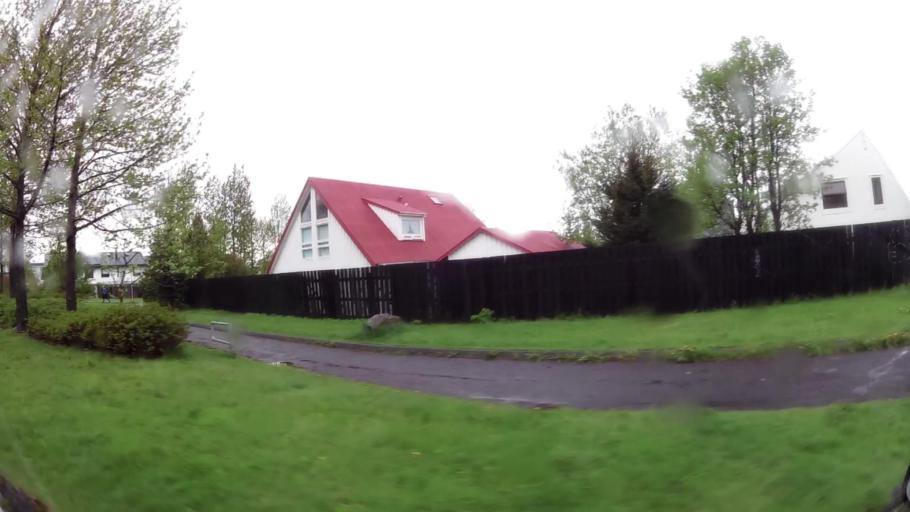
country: IS
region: Capital Region
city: Reykjavik
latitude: 64.0969
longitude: -21.8366
